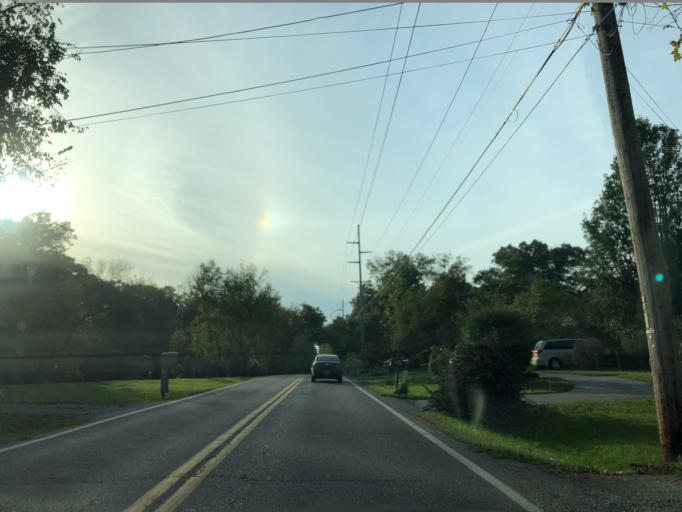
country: US
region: Ohio
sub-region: Warren County
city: Loveland Park
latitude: 39.2888
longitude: -84.2688
